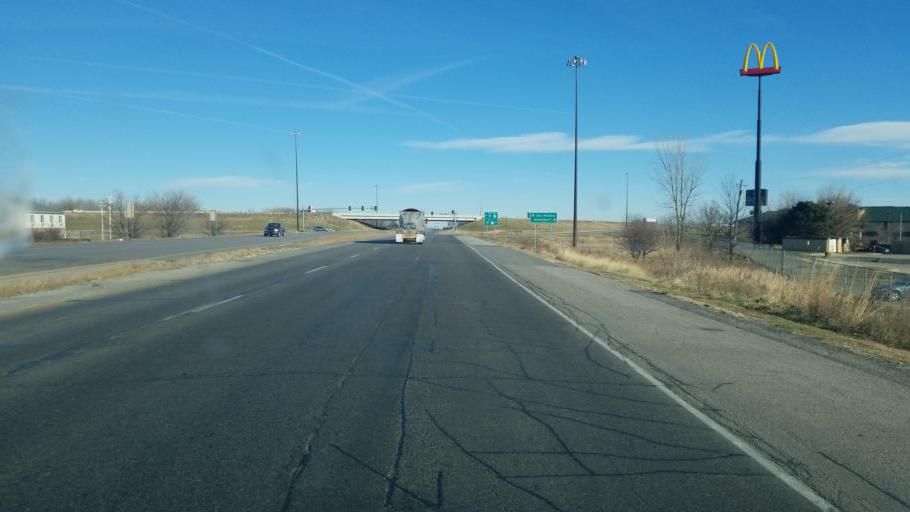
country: US
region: Iowa
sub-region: Polk County
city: Altoona
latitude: 41.6591
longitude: -93.4978
